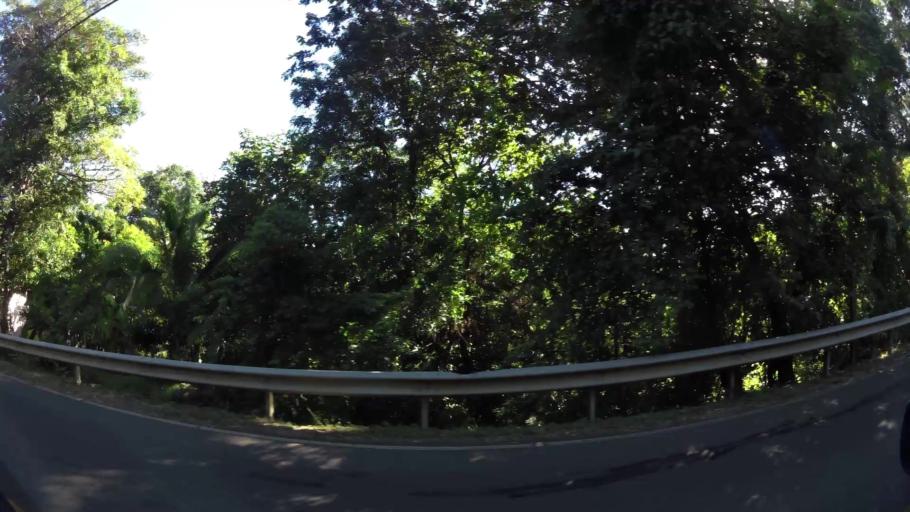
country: CR
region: Guanacaste
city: Belen
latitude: 10.3879
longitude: -85.6196
